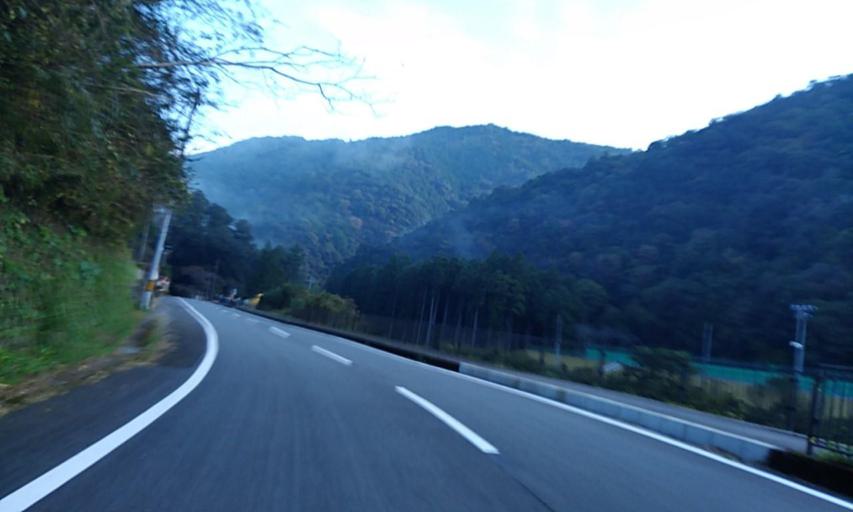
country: JP
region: Wakayama
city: Shingu
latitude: 33.7306
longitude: 135.9104
